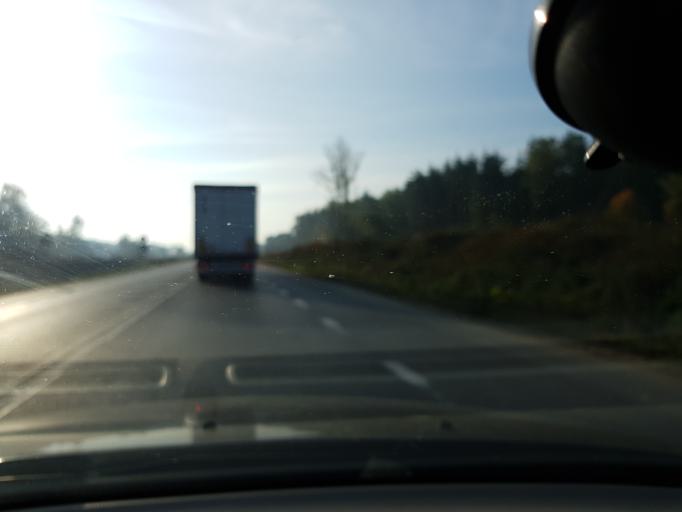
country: PL
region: Masovian Voivodeship
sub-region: Powiat otwocki
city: Otwock
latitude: 52.1623
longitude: 21.3018
